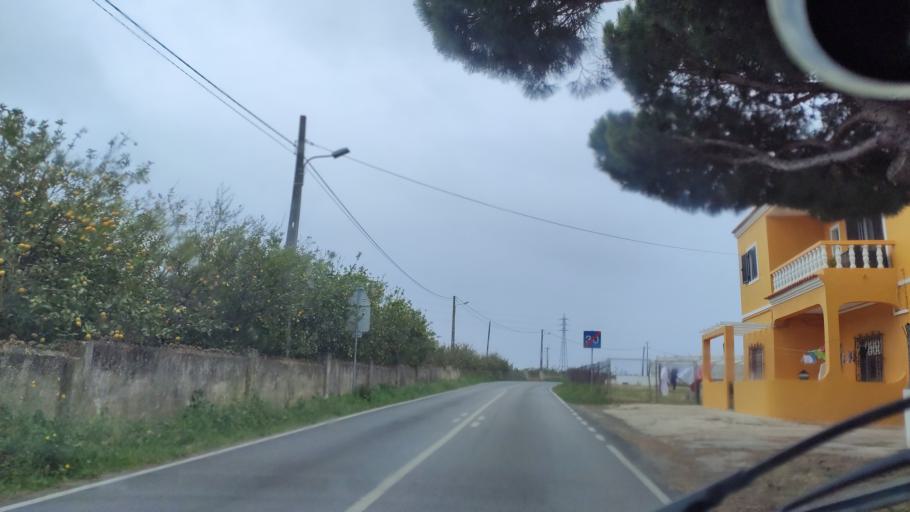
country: PT
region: Faro
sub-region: Faro
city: Santa Barbara de Nexe
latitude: 37.0733
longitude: -7.9391
